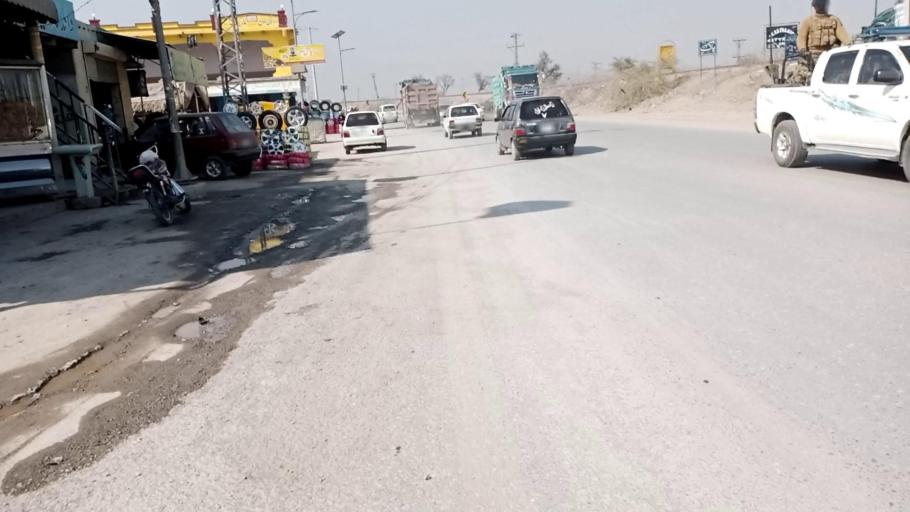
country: PK
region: Khyber Pakhtunkhwa
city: Peshawar
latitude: 34.0009
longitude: 71.3989
